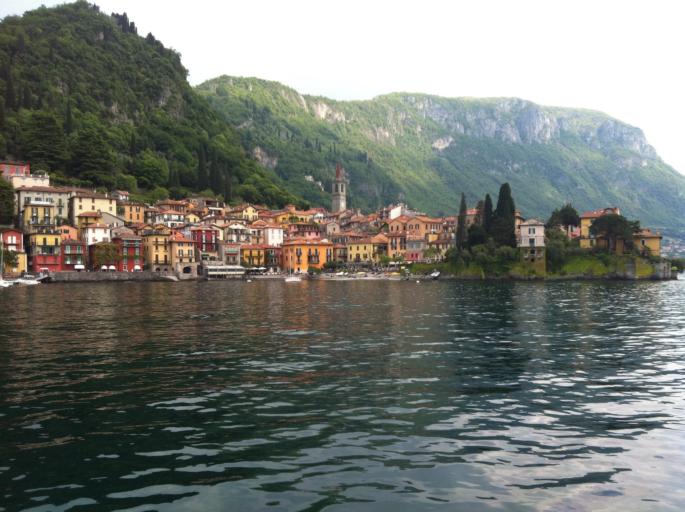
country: IT
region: Lombardy
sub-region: Provincia di Lecco
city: Varenna
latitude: 46.0118
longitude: 9.2802
